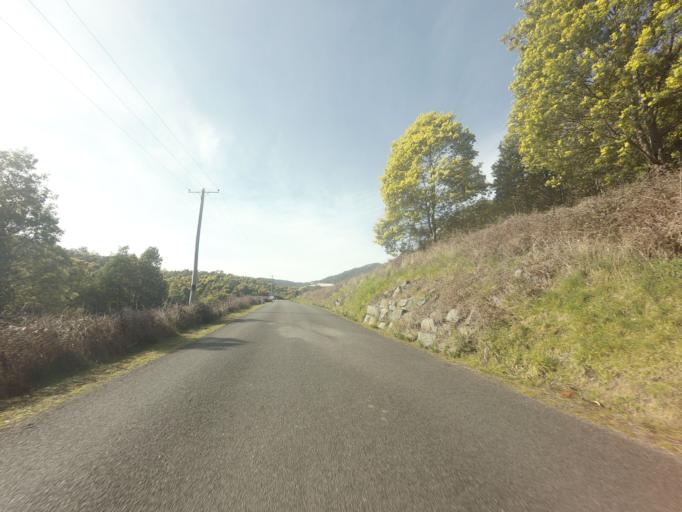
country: AU
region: Tasmania
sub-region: Huon Valley
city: Cygnet
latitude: -43.1755
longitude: 147.1526
